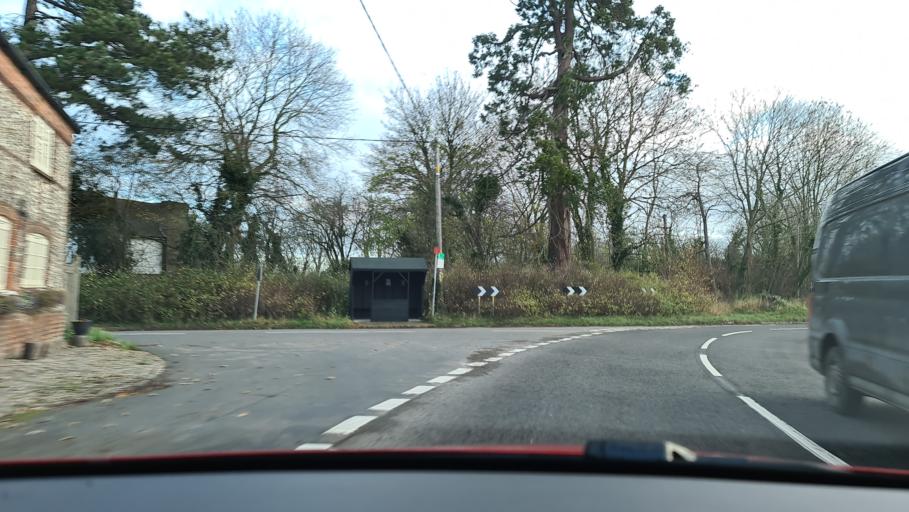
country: GB
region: England
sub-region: Oxfordshire
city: Chinnor
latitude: 51.7207
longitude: -0.8751
